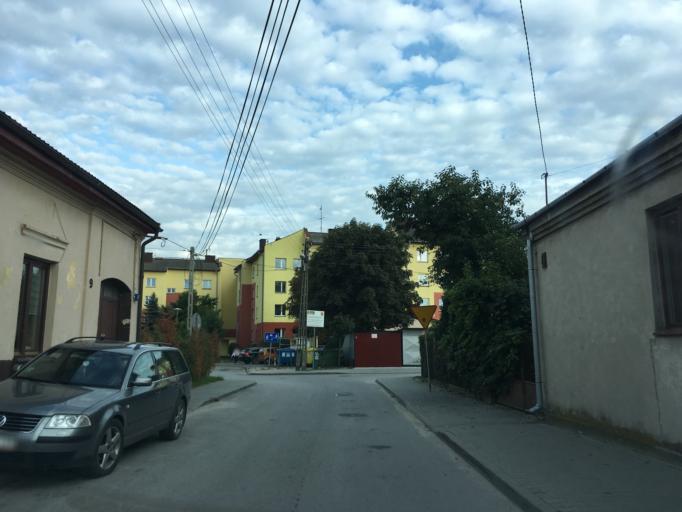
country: PL
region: Swietokrzyskie
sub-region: Powiat wloszczowski
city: Wloszczowa
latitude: 50.8501
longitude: 19.9671
